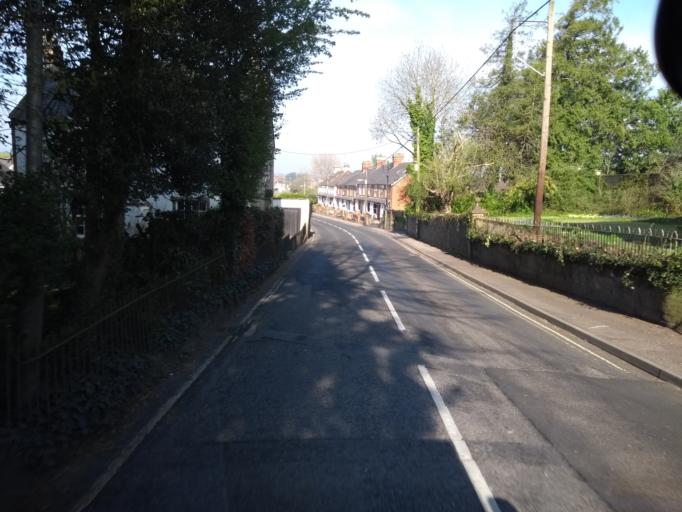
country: GB
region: England
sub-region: Somerset
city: Ilminster
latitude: 50.9292
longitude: -2.9200
